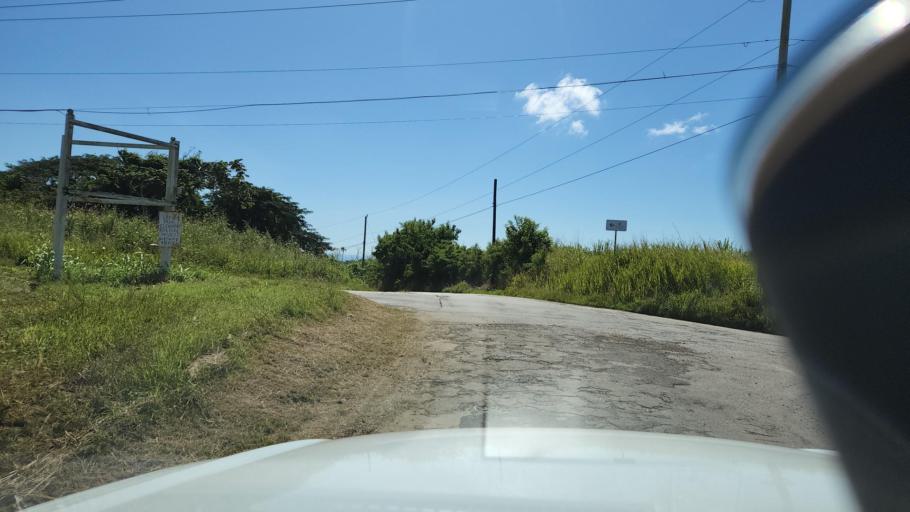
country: BB
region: Saint Thomas
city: Welchman Hall
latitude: 13.1881
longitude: -59.5937
